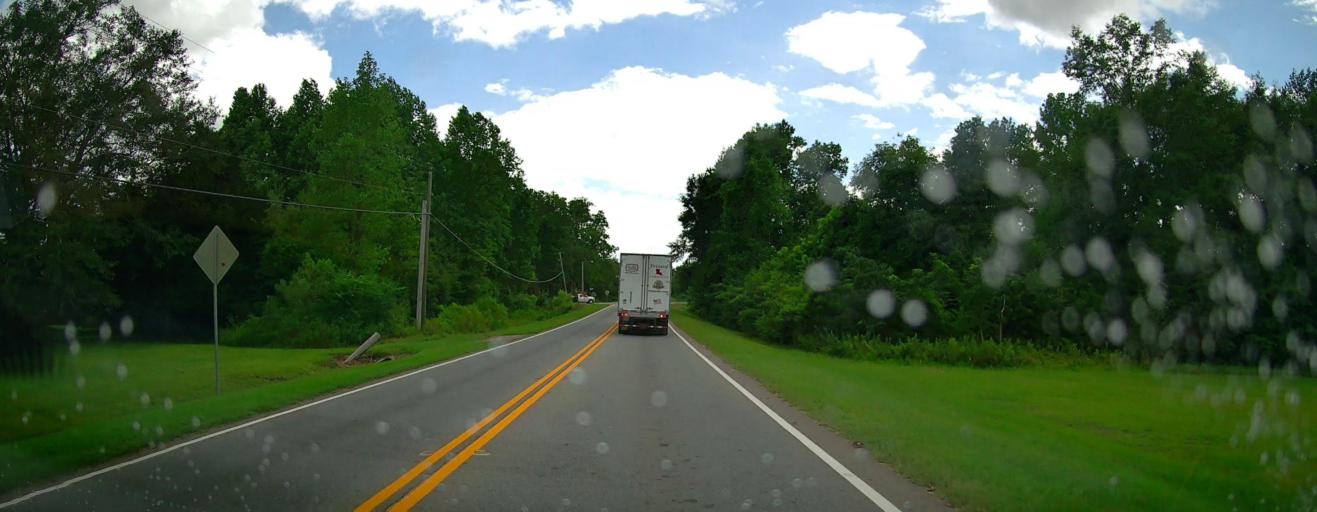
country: US
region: Georgia
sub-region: Ben Hill County
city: Fitzgerald
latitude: 31.7083
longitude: -83.2368
